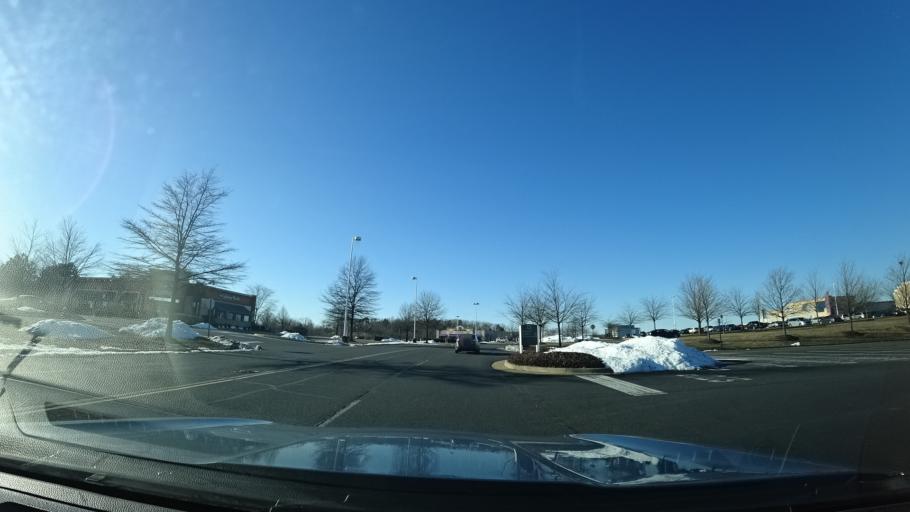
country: US
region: Virginia
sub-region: Loudoun County
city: Dulles Town Center
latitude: 39.0296
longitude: -77.4248
